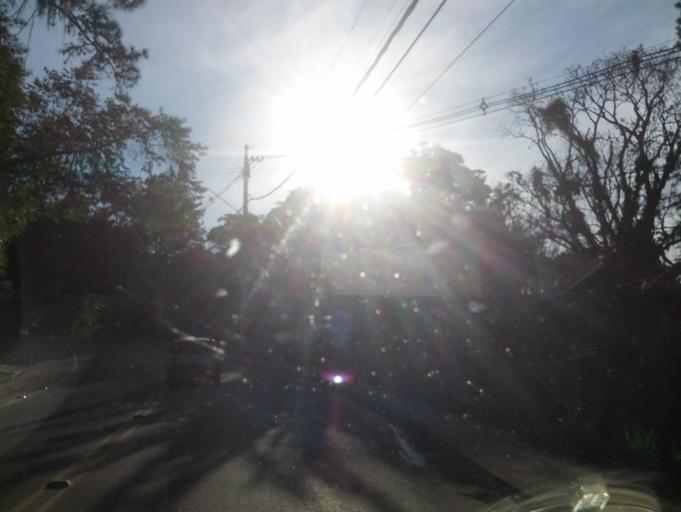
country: BR
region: Santa Catarina
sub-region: Blumenau
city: Blumenau
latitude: -26.9089
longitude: -49.1476
